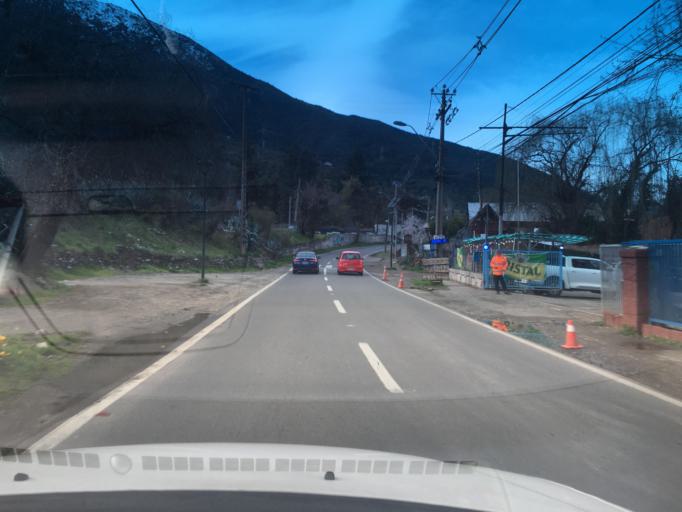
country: CL
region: Santiago Metropolitan
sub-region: Provincia de Cordillera
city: Puente Alto
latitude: -33.5913
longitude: -70.4849
